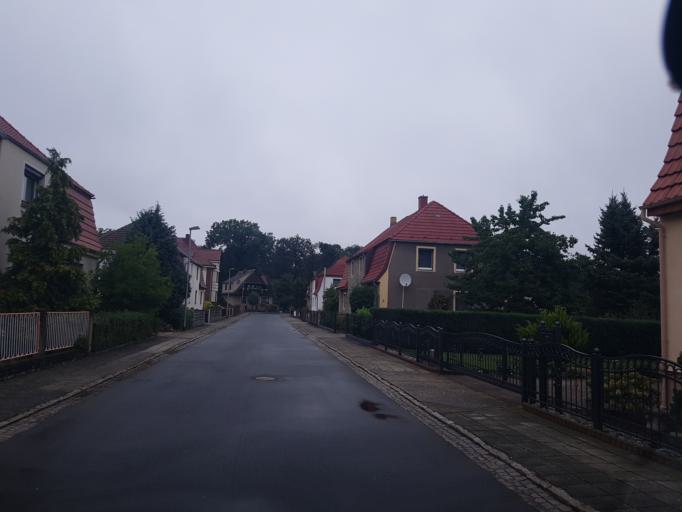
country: DE
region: Brandenburg
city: Elsterwerda
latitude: 51.4502
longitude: 13.5214
